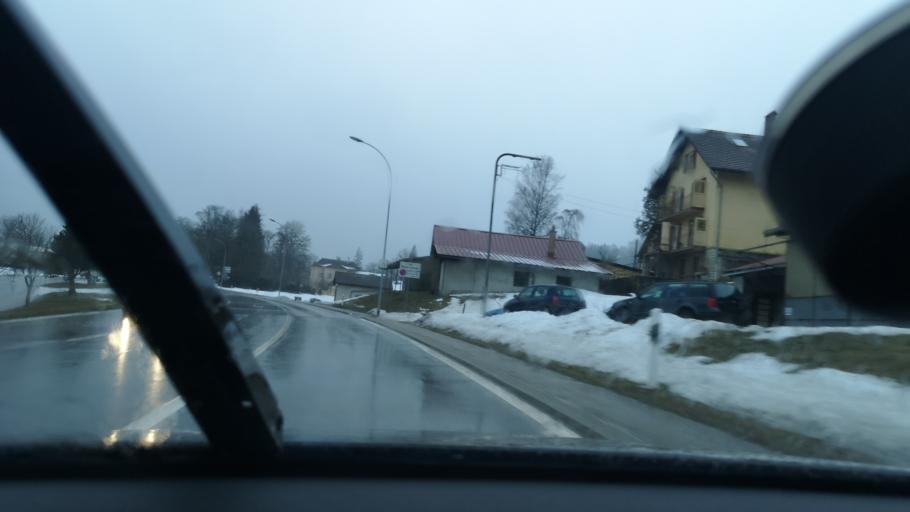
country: CH
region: Neuchatel
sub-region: Val-de-Travers District
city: Couvet
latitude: 46.9305
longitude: 6.6387
